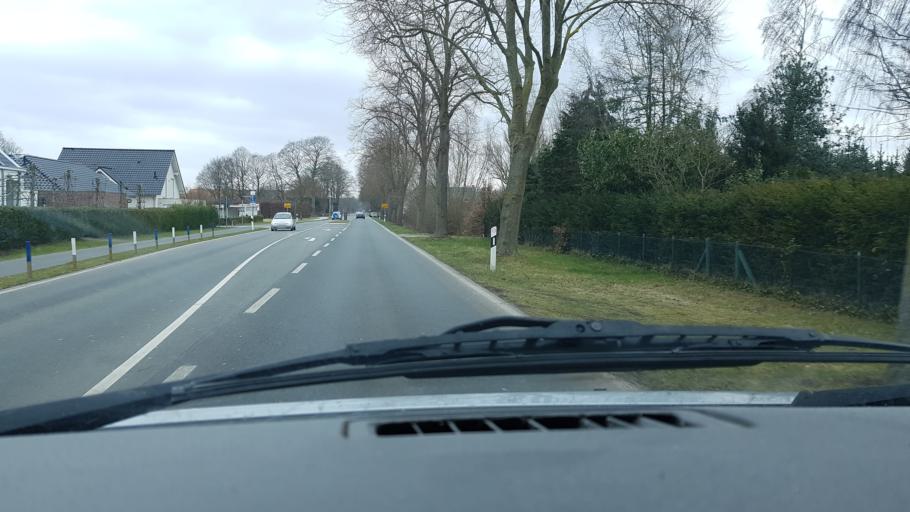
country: DE
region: North Rhine-Westphalia
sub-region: Regierungsbezirk Dusseldorf
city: Kranenburg
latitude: 51.7924
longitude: 5.9981
